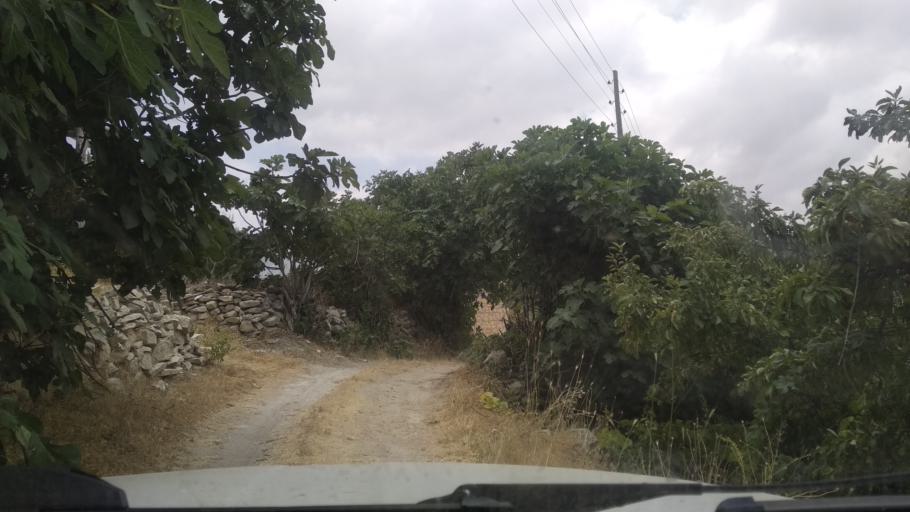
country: TR
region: Mersin
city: Sarikavak
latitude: 36.6002
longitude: 33.7263
